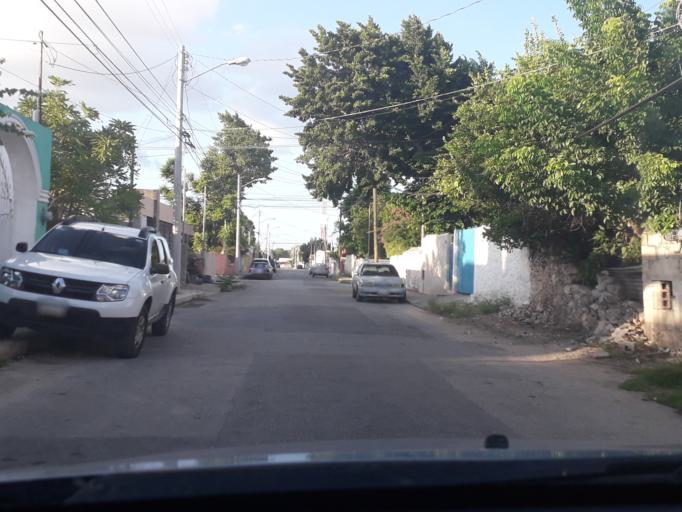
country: MX
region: Yucatan
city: Merida
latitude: 20.9683
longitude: -89.6458
